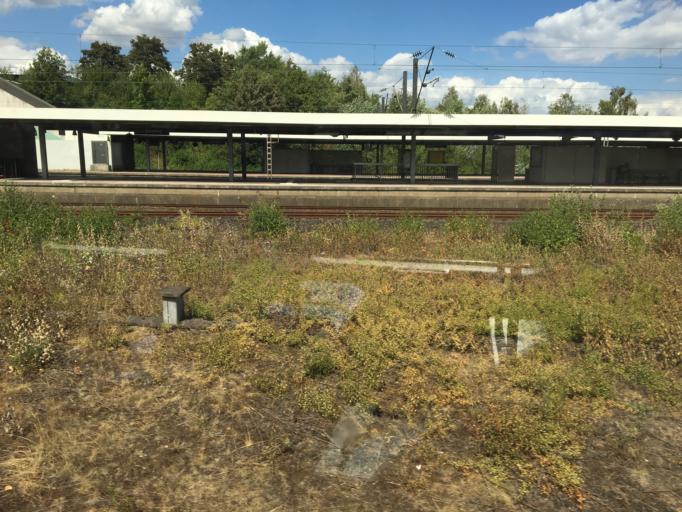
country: DE
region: North Rhine-Westphalia
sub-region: Regierungsbezirk Arnsberg
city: Dortmund
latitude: 51.5091
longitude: 7.4250
